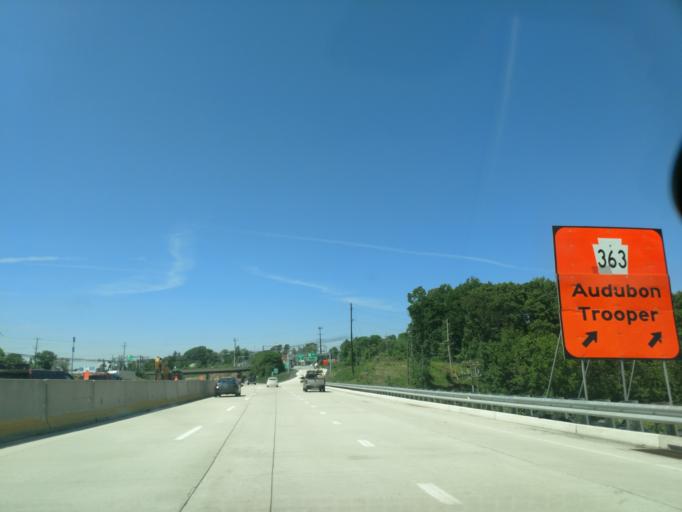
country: US
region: Pennsylvania
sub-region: Montgomery County
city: Audubon
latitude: 40.1096
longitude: -75.4198
